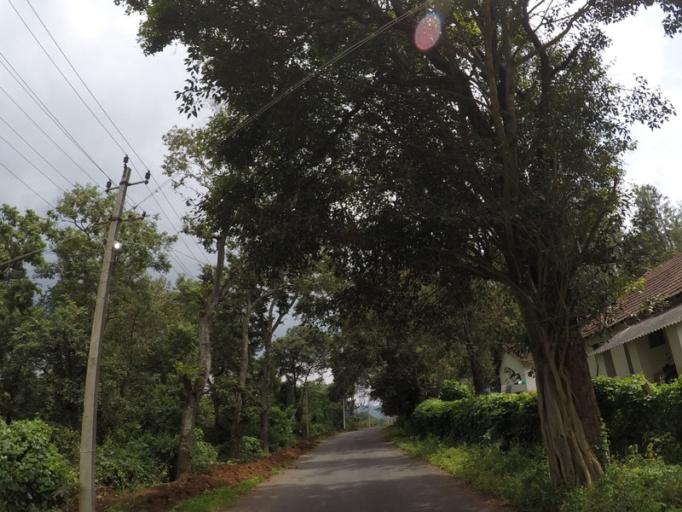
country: IN
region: Karnataka
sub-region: Chikmagalur
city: Chikmagalur
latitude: 13.4387
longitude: 75.8054
